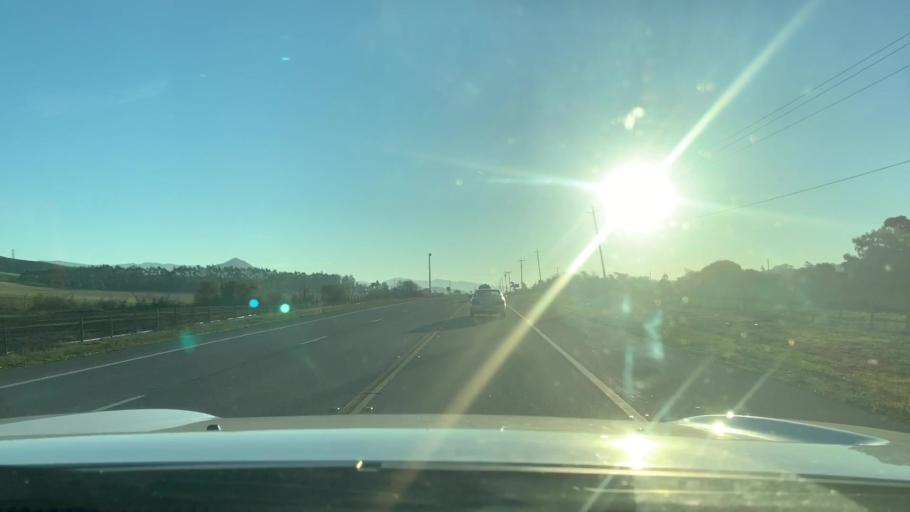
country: US
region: California
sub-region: San Luis Obispo County
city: San Luis Obispo
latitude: 35.2887
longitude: -120.7451
